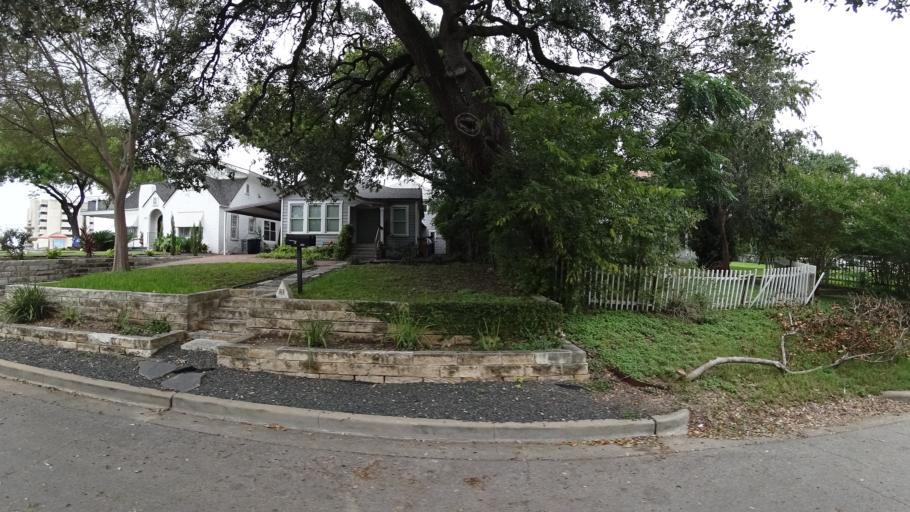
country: US
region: Texas
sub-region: Travis County
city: Austin
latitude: 30.2731
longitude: -97.7307
